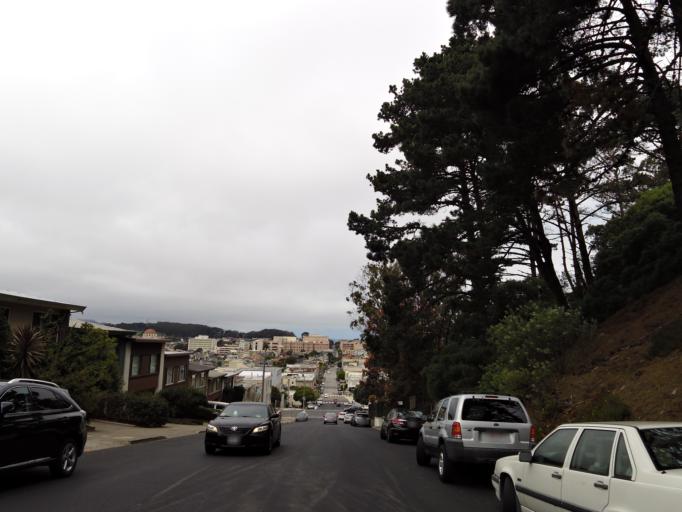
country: US
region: California
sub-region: San Francisco County
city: San Francisco
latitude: 37.7792
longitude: -122.4537
